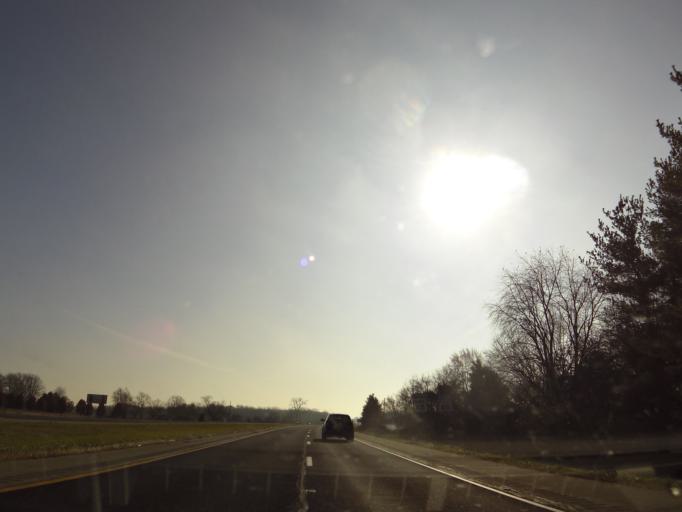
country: US
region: Indiana
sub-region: Marion County
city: Cumberland
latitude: 39.7089
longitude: -86.0010
